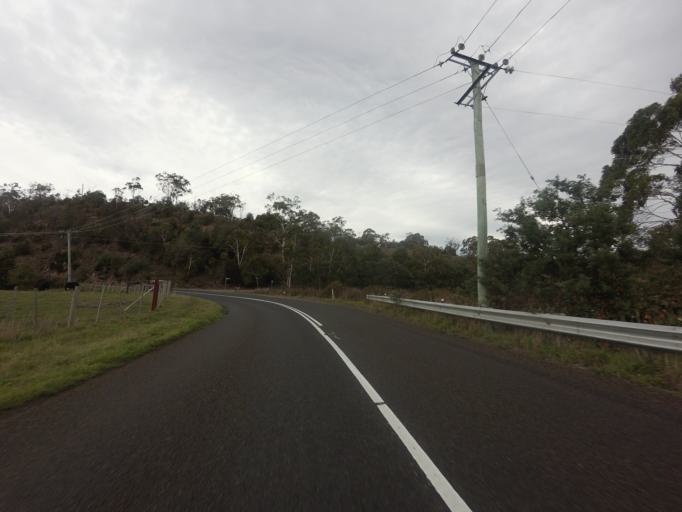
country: AU
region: Tasmania
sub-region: Brighton
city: Bridgewater
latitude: -42.6767
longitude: 147.1566
